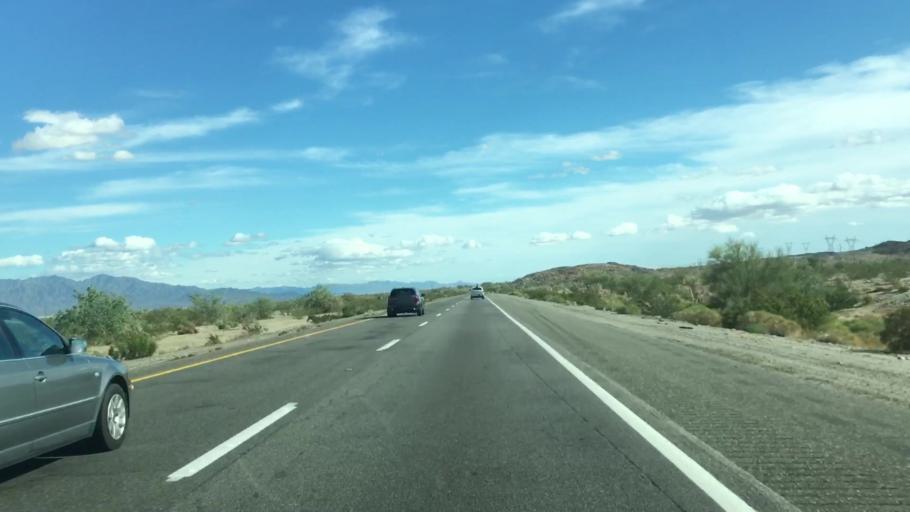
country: US
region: California
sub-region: Imperial County
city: Niland
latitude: 33.7079
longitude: -115.3597
